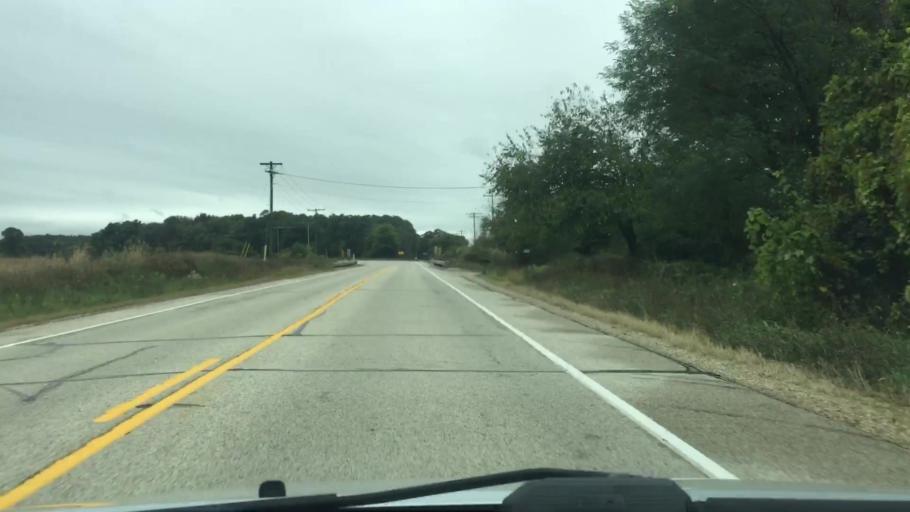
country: US
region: Wisconsin
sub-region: Jefferson County
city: Palmyra
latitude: 42.8194
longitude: -88.5602
